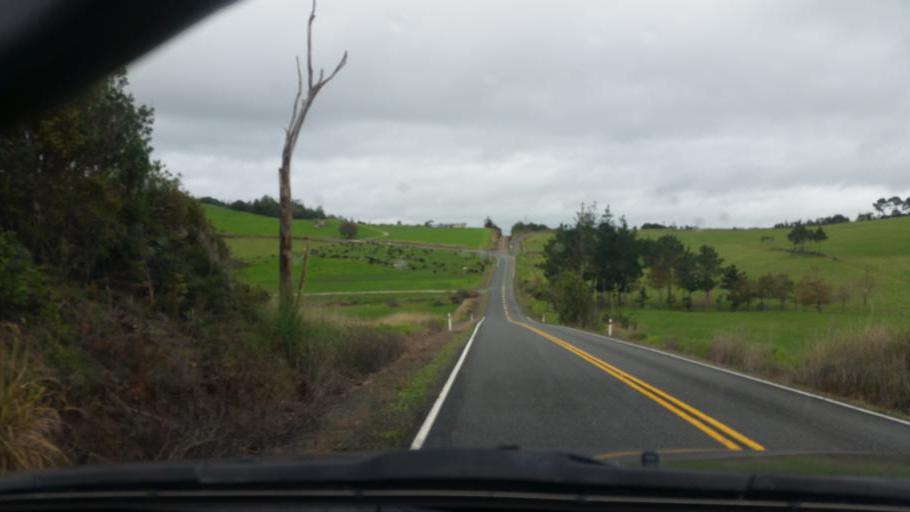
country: NZ
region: Northland
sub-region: Kaipara District
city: Dargaville
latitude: -36.0203
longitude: 173.9850
